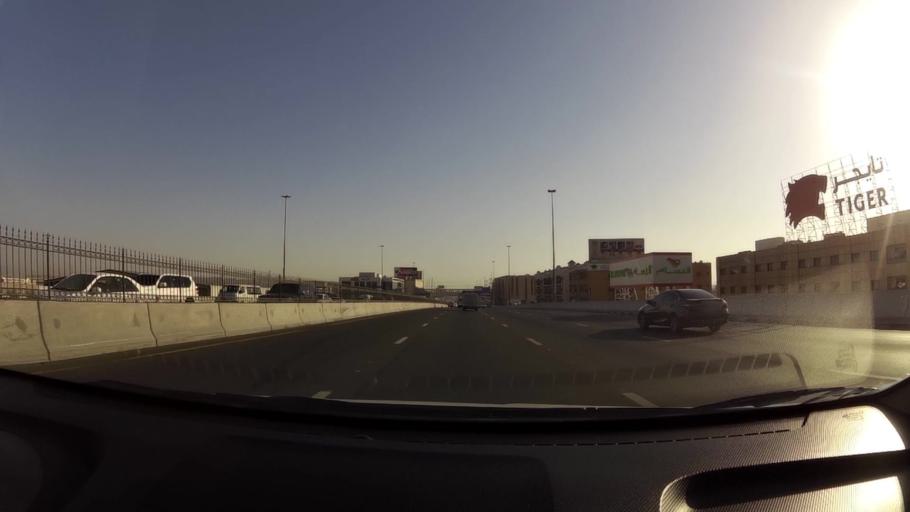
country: AE
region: Ash Shariqah
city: Sharjah
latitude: 25.2960
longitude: 55.4363
